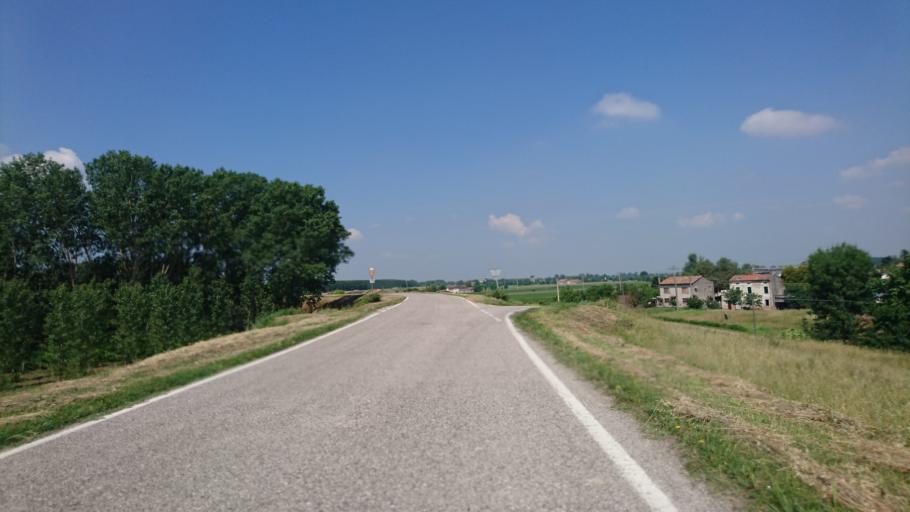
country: IT
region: Lombardy
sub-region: Provincia di Mantova
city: Sustinente
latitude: 45.0707
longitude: 10.9936
